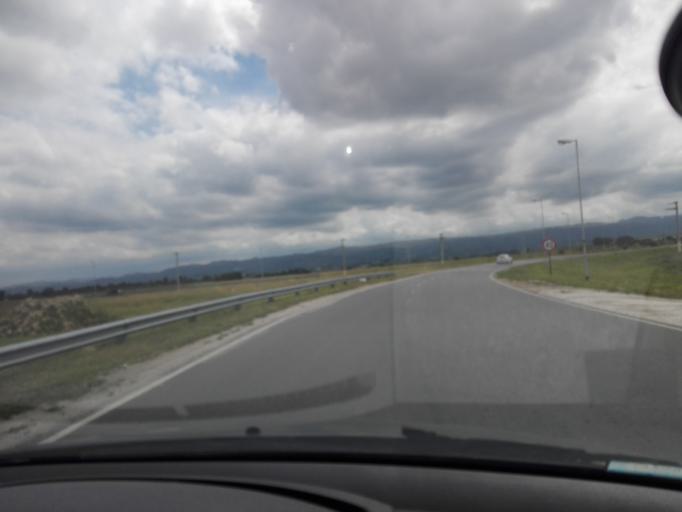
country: AR
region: Cordoba
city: Alta Gracia
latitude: -31.6364
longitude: -64.4041
